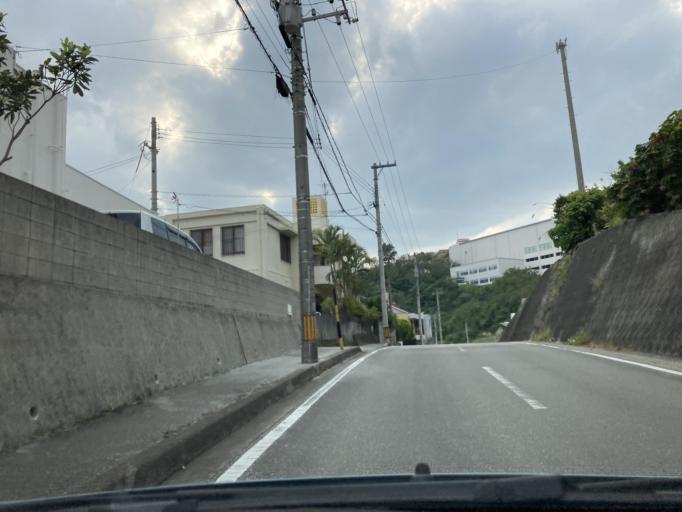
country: JP
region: Okinawa
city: Naha-shi
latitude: 26.2079
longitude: 127.7313
